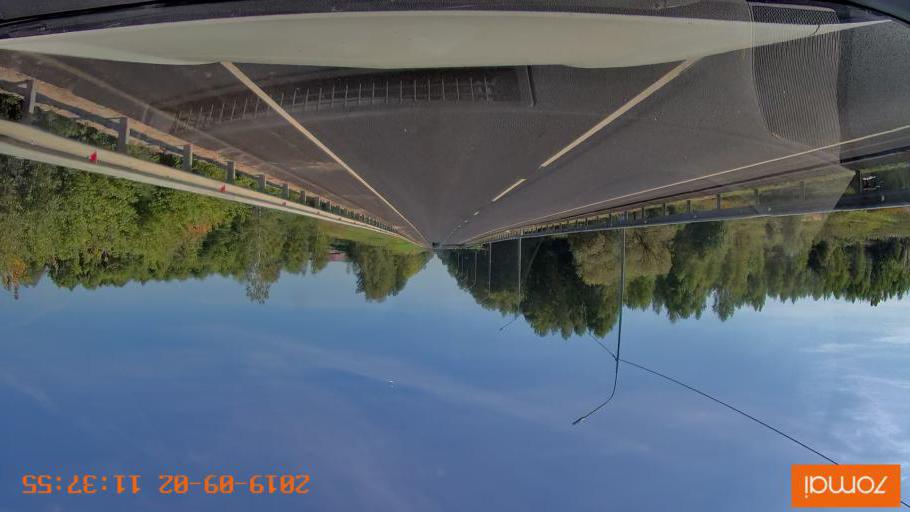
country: RU
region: Smolensk
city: Oster
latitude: 53.9161
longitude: 32.7501
